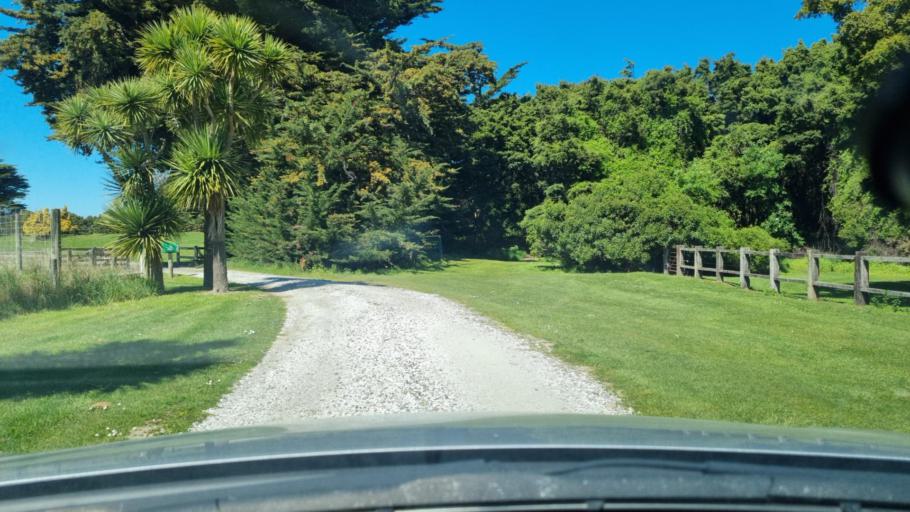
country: NZ
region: Southland
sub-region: Invercargill City
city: Invercargill
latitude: -46.4572
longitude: 168.2813
